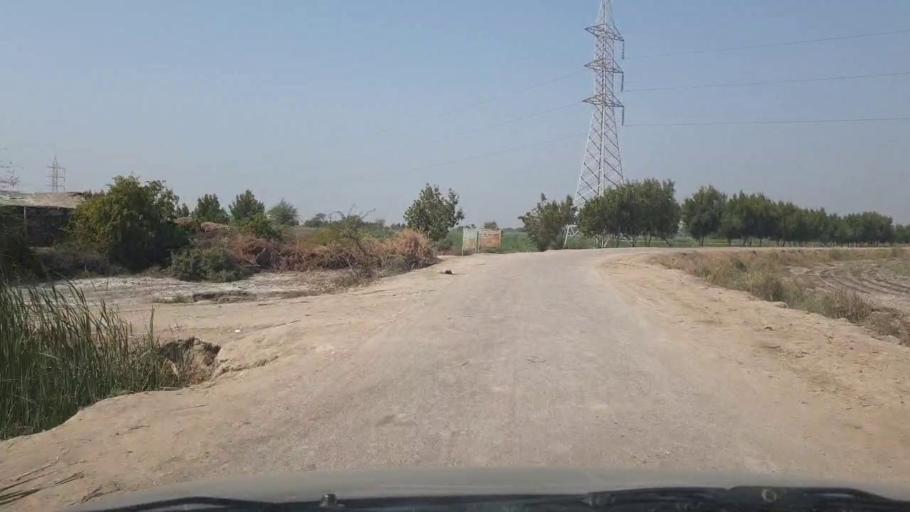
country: PK
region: Sindh
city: Mirwah Gorchani
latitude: 25.3167
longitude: 69.1541
